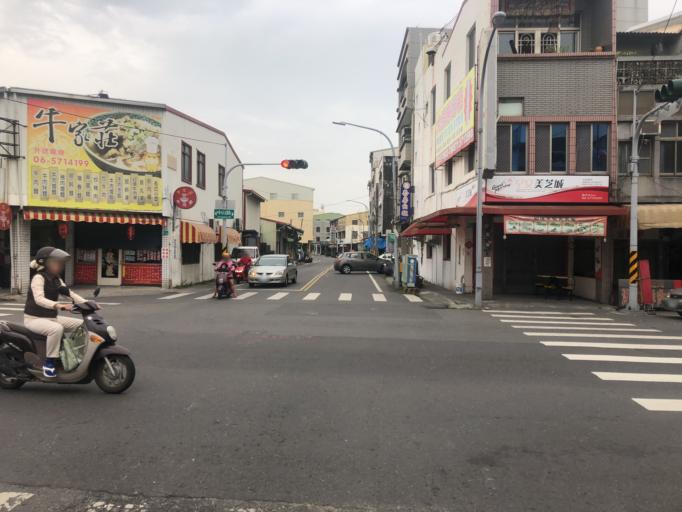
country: TW
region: Taiwan
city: Xinying
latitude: 23.1835
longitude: 120.2445
